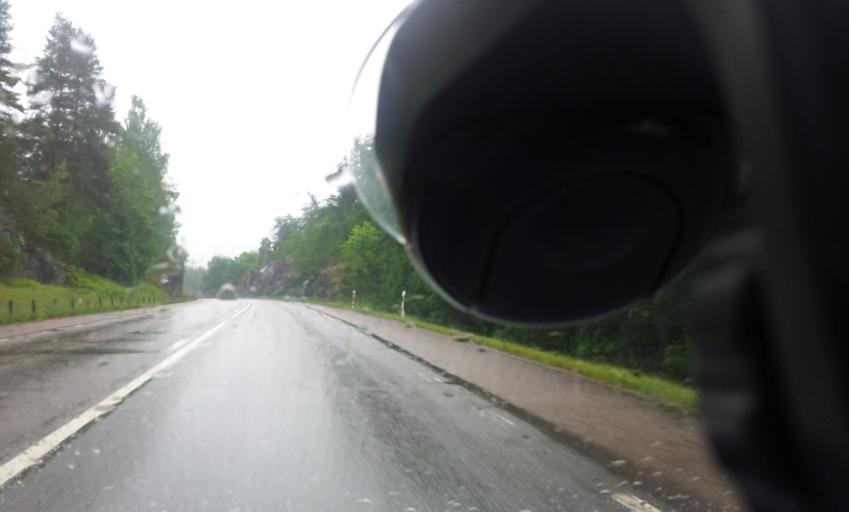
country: SE
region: Kalmar
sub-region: Vasterviks Kommun
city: Ankarsrum
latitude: 57.6700
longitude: 16.4418
